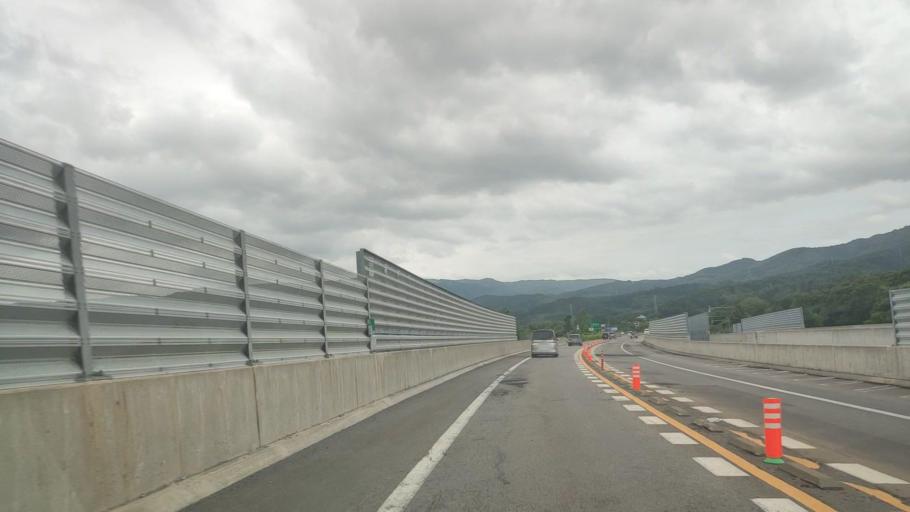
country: JP
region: Hokkaido
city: Nanae
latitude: 41.9171
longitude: 140.6833
